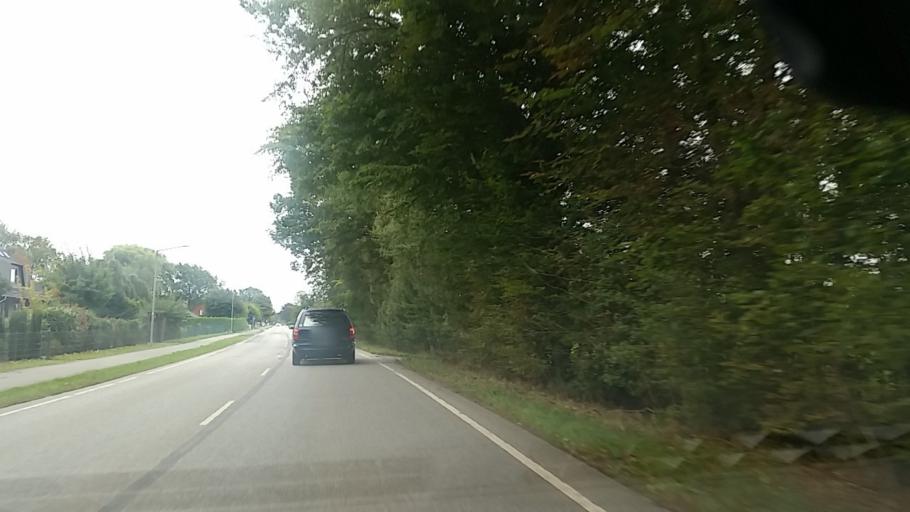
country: DE
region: Schleswig-Holstein
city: Kayhude
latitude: 53.7693
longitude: 10.1243
